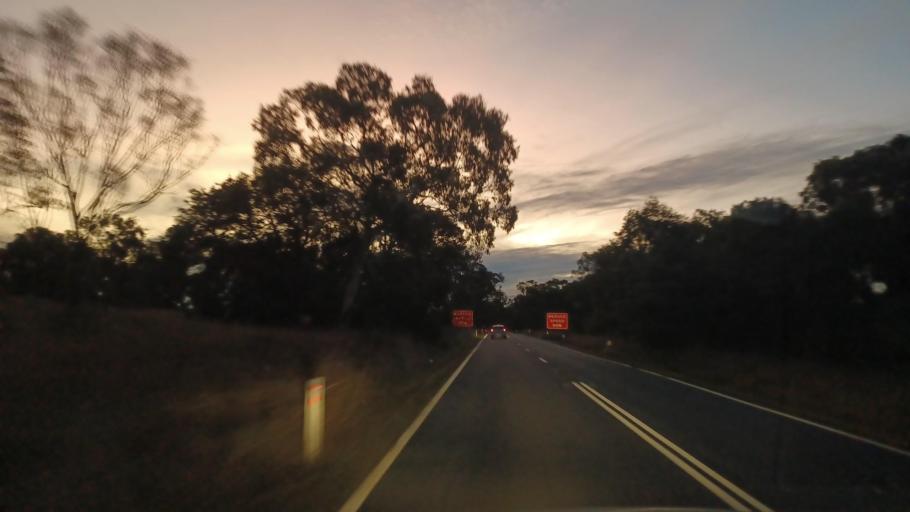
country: AU
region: Australian Capital Territory
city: Belconnen
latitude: -35.1903
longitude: 149.0597
